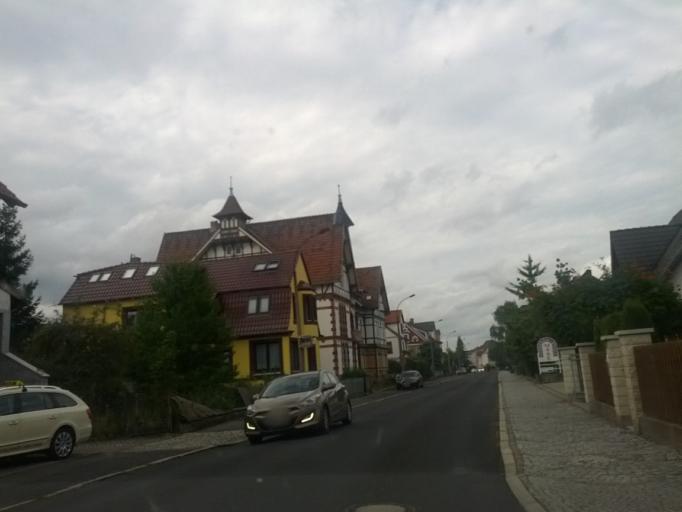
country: DE
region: Thuringia
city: Bad Salzungen
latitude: 50.8130
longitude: 10.2457
